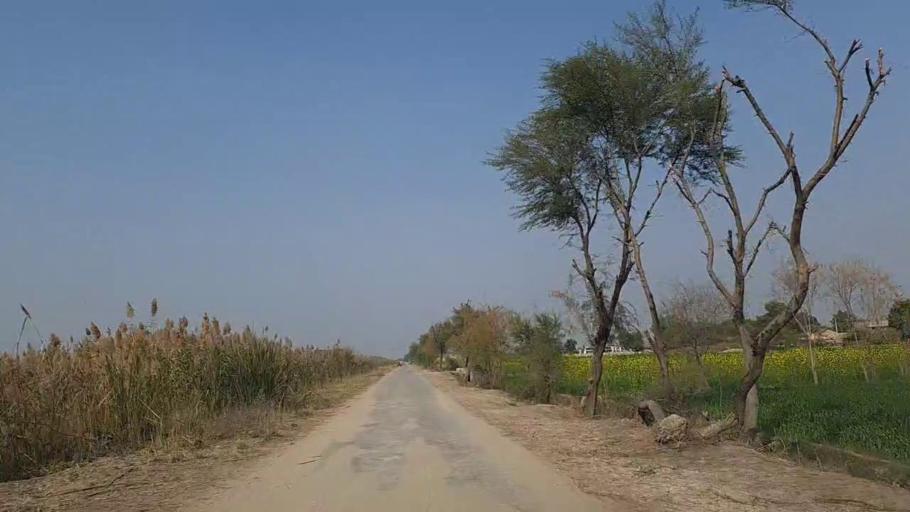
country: PK
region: Sindh
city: Daur
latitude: 26.4707
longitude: 68.4665
